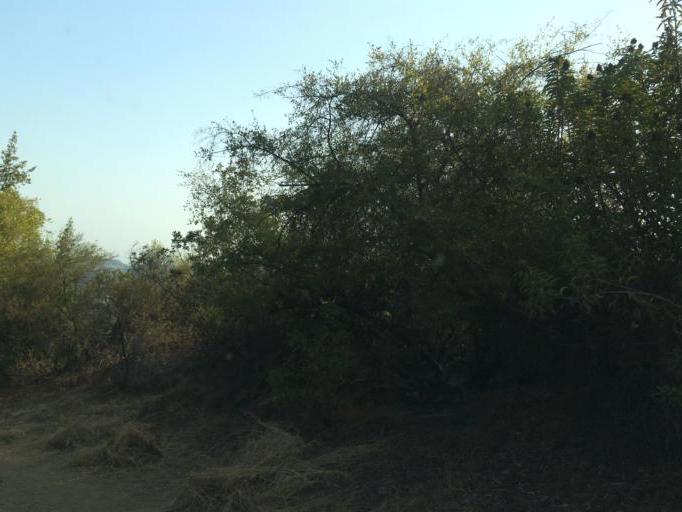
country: US
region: California
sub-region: Los Angeles County
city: Topanga
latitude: 34.0719
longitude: -118.5997
